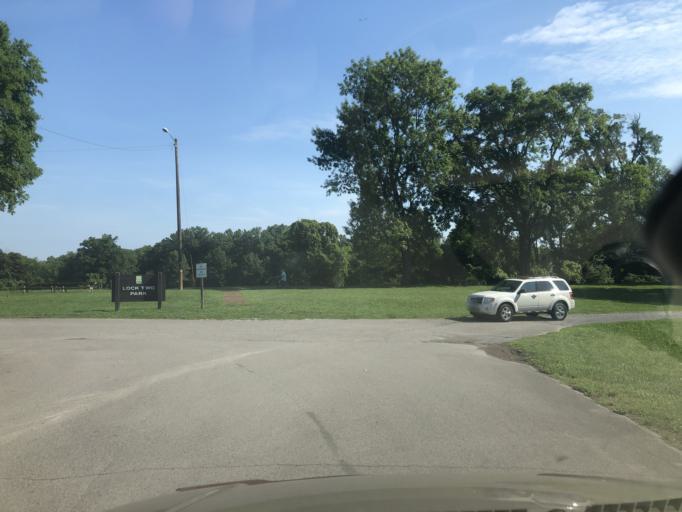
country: US
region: Tennessee
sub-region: Davidson County
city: Lakewood
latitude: 36.2439
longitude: -86.7019
